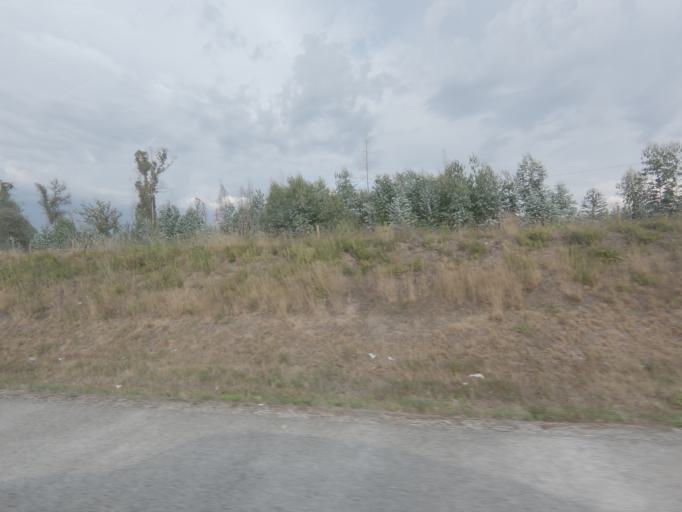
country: PT
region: Viseu
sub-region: Santa Comba Dao
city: Santa Comba Dao
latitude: 40.4561
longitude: -8.1036
